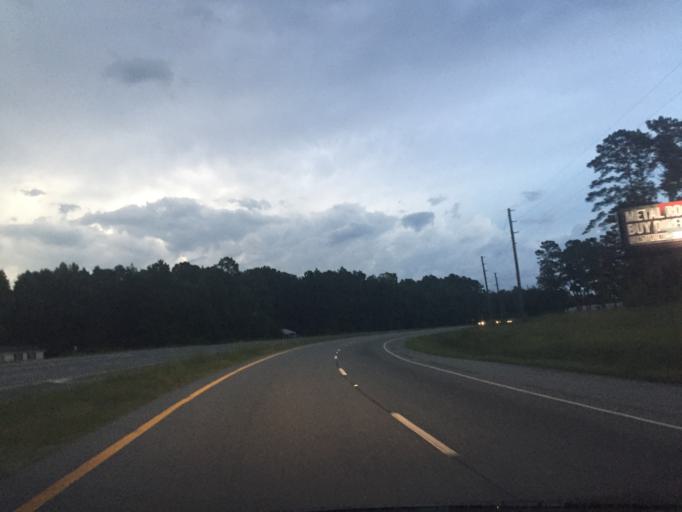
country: US
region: Georgia
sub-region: Liberty County
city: Hinesville
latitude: 31.8255
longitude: -81.5172
